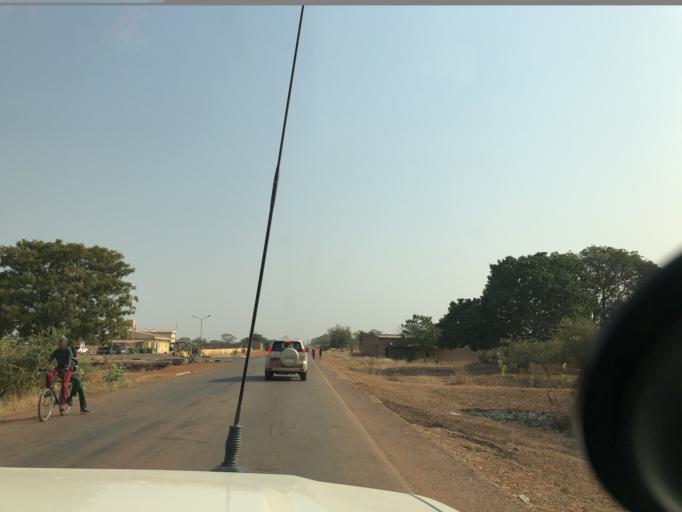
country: TD
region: Logone Occidental
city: Moundou
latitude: 8.5881
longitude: 16.0236
